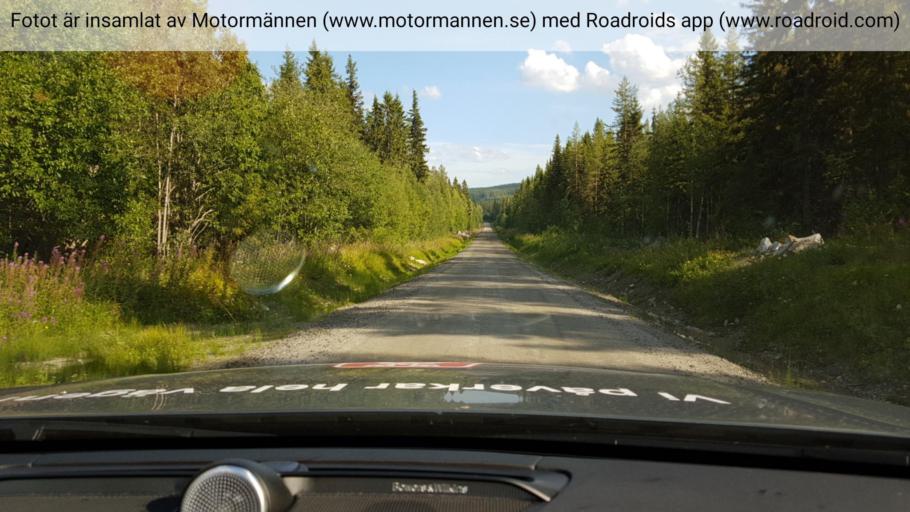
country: SE
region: Vaesterbotten
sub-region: Dorotea Kommun
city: Dorotea
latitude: 63.9281
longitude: 16.1663
